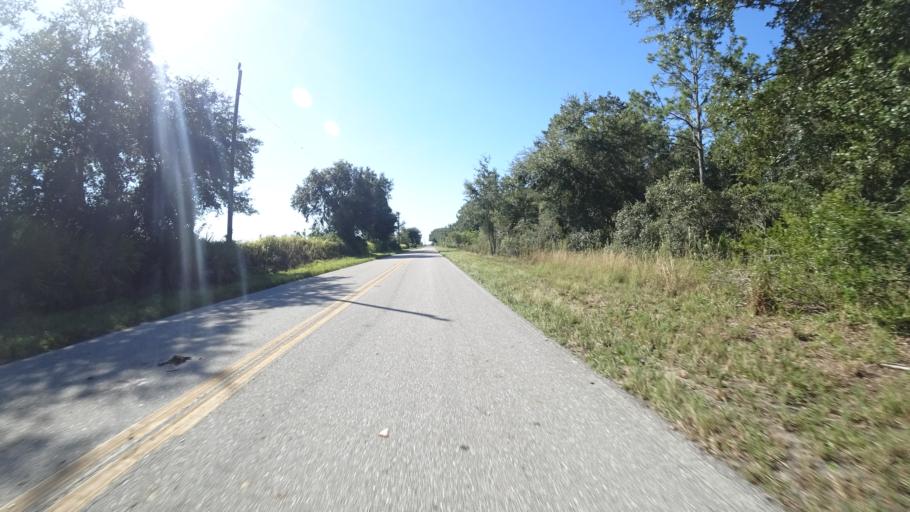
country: US
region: Florida
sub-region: Hillsborough County
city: Wimauma
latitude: 27.6253
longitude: -82.2925
